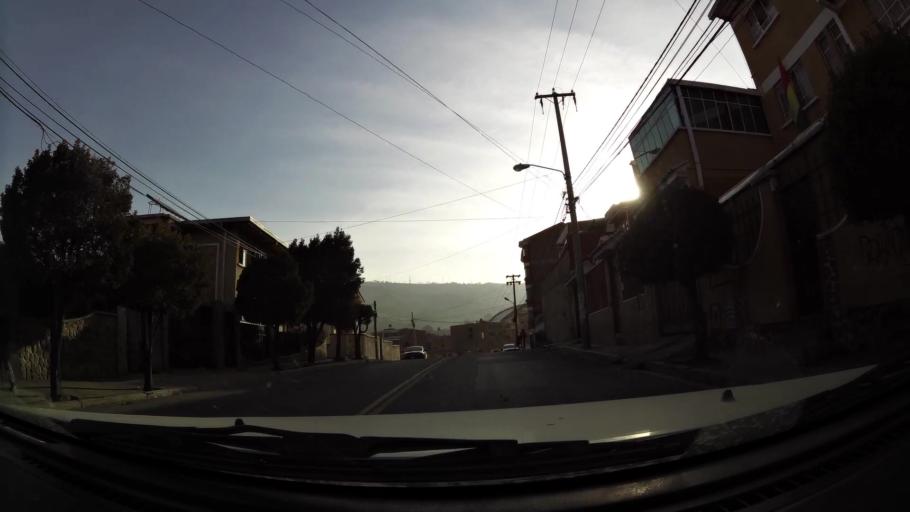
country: BO
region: La Paz
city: La Paz
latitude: -16.5202
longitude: -68.1088
